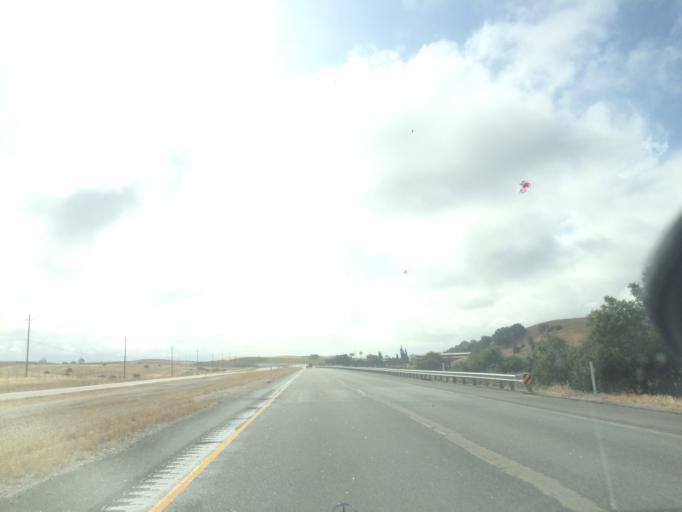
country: US
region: California
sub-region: San Luis Obispo County
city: Paso Robles
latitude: 35.6580
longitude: -120.5419
